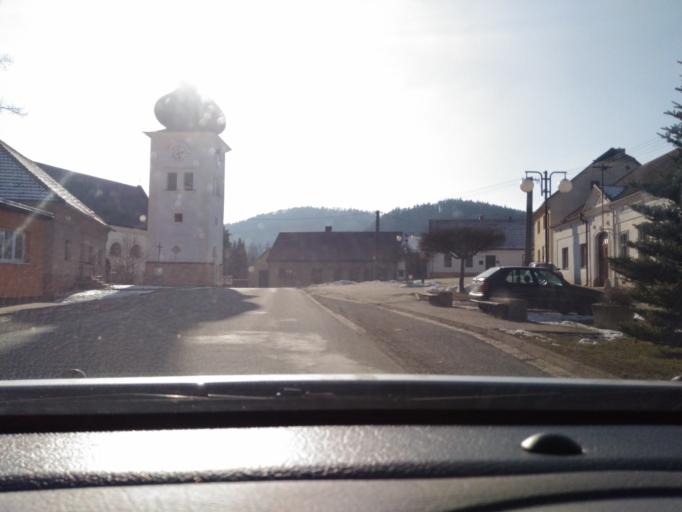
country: CZ
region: South Moravian
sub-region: Okres Brno-Venkov
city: Nedvedice
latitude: 49.5048
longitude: 16.3392
